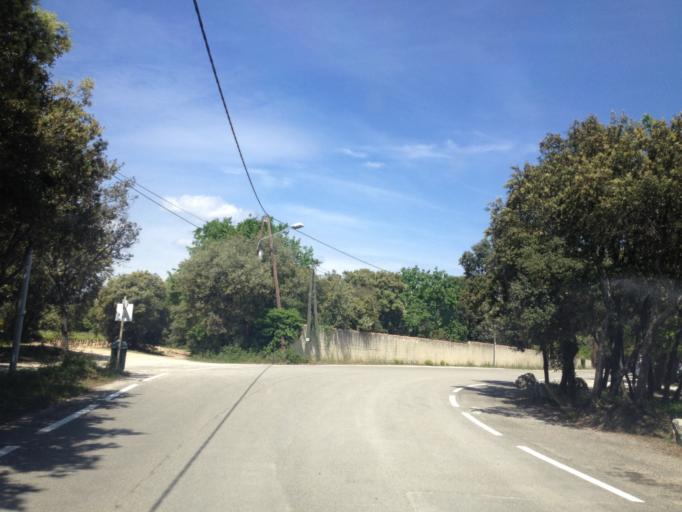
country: FR
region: Provence-Alpes-Cote d'Azur
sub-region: Departement du Vaucluse
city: Orange
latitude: 44.1132
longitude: 4.8263
